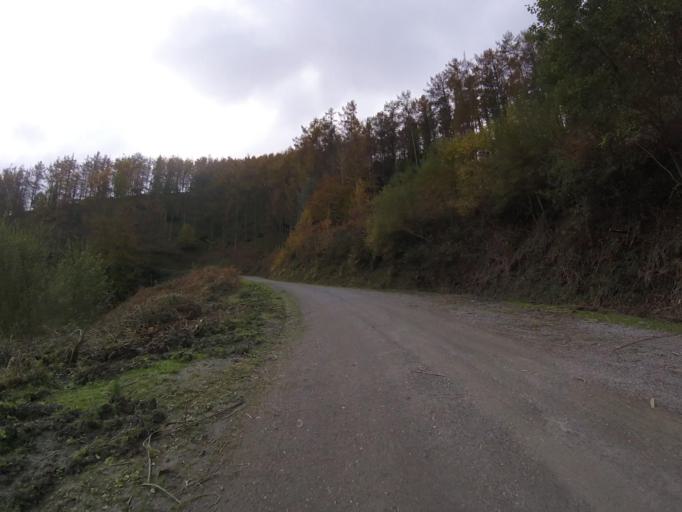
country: ES
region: Navarre
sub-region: Provincia de Navarra
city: Goizueta
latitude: 43.2179
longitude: -1.8224
